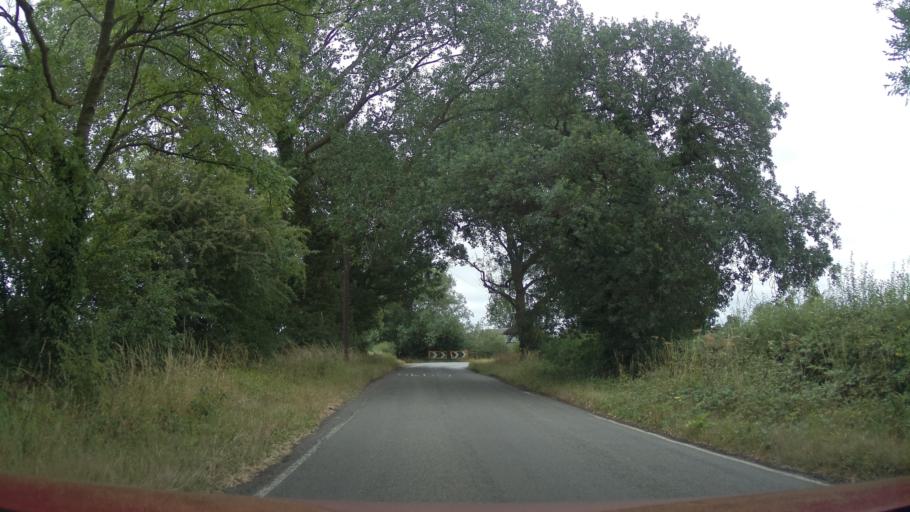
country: GB
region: England
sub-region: Derbyshire
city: Findern
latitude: 52.8834
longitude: -1.5295
